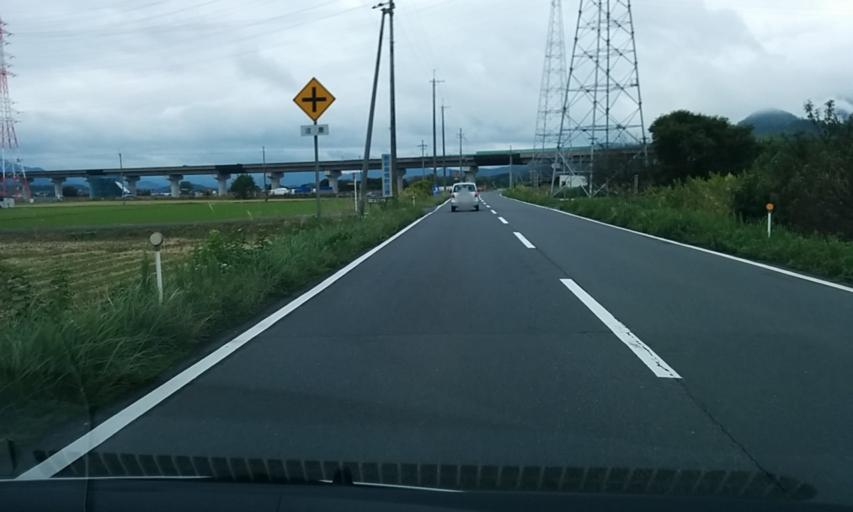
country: JP
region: Kyoto
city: Ayabe
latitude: 35.3066
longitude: 135.1950
